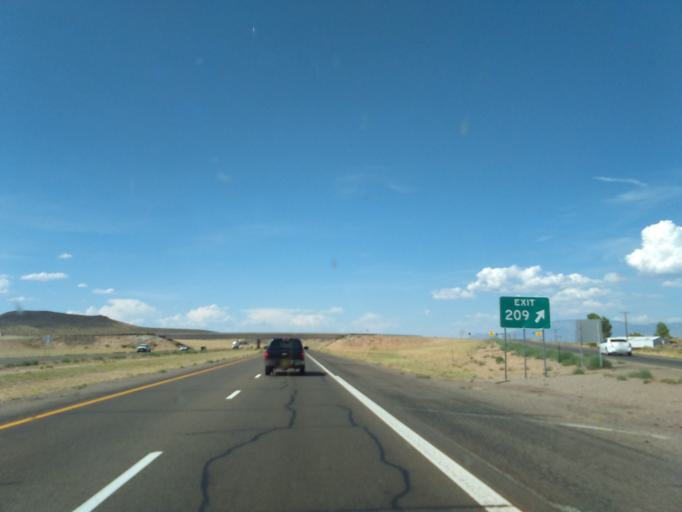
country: US
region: New Mexico
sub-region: Valencia County
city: Bosque Farms
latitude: 34.9018
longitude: -106.7248
